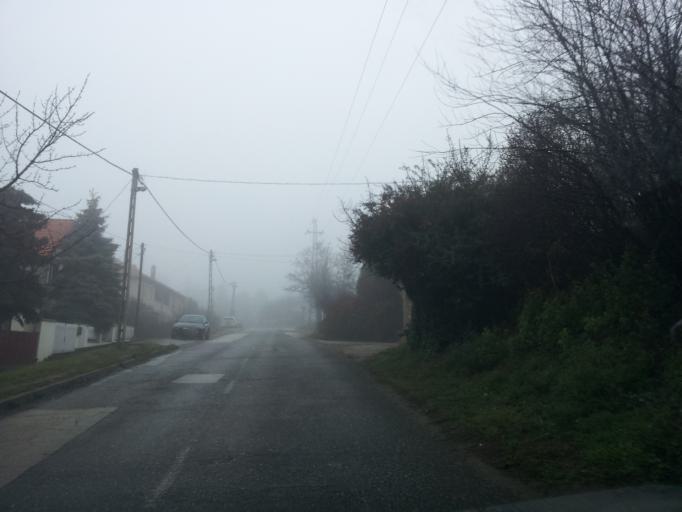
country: HU
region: Pest
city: Erd
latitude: 47.3964
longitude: 18.9211
